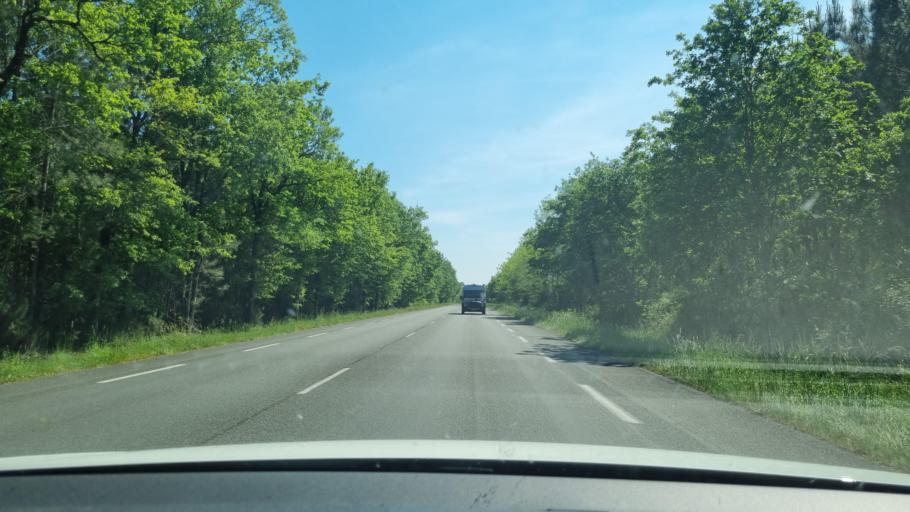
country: FR
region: Aquitaine
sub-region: Departement des Landes
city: Roquefort
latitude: 44.2184
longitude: -0.2648
